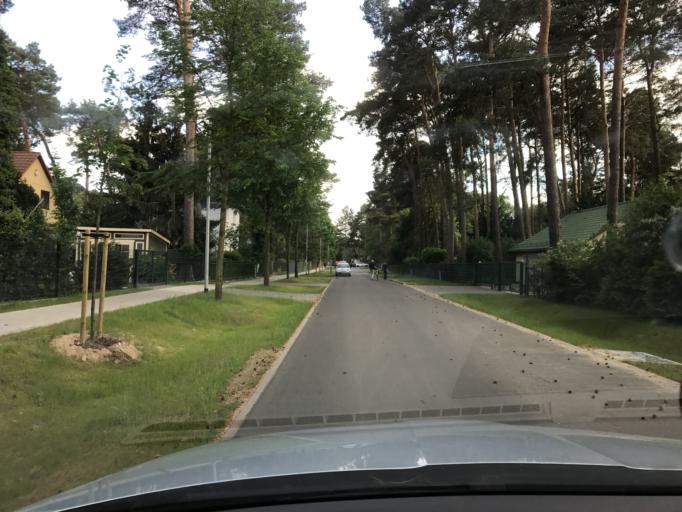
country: DE
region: Brandenburg
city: Falkensee
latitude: 52.5708
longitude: 13.0793
